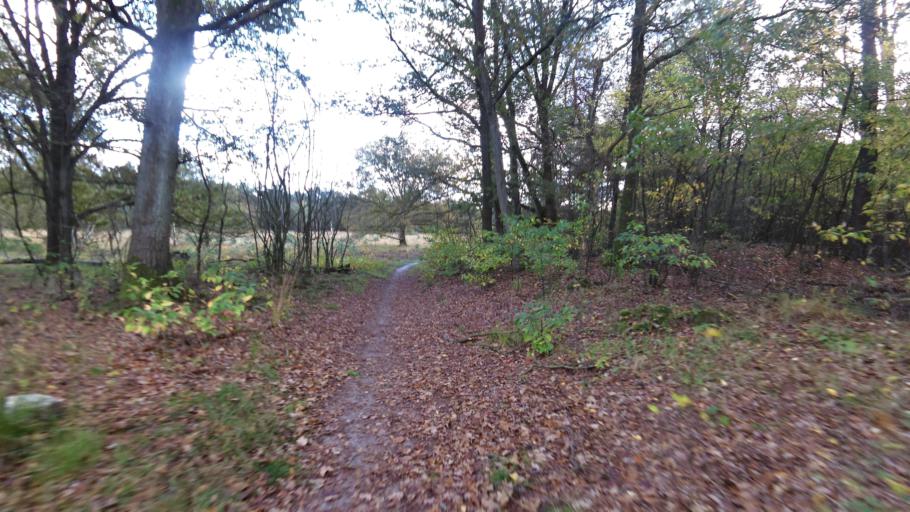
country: NL
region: Gelderland
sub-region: Gemeente Nunspeet
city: Nunspeet
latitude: 52.3647
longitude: 5.8310
